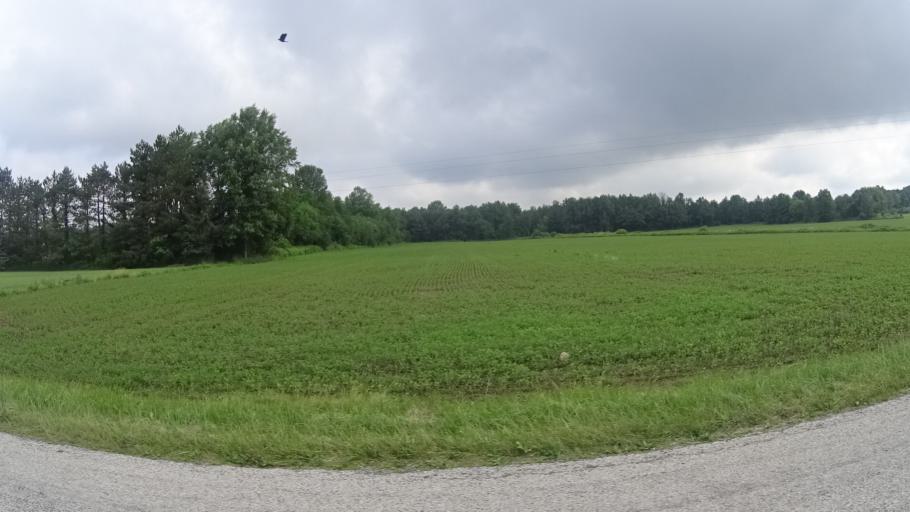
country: US
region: Ohio
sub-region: Huron County
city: Wakeman
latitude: 41.2840
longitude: -82.4523
